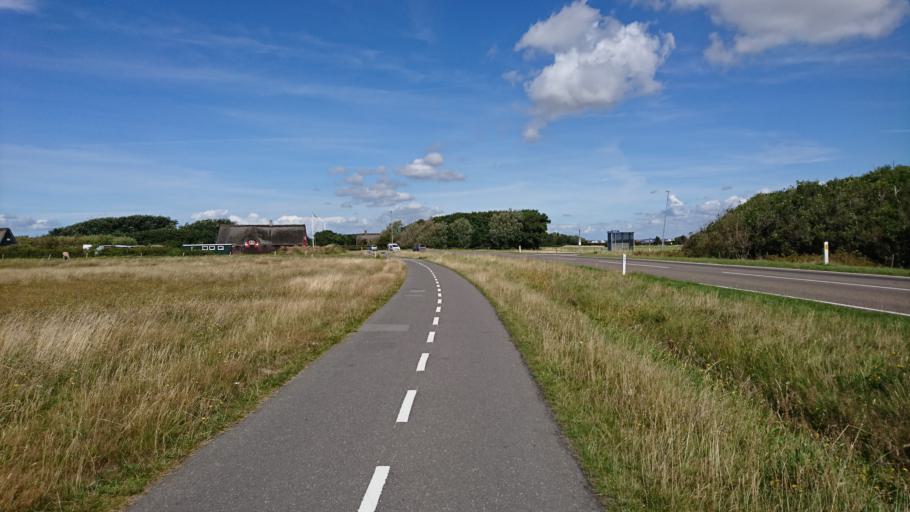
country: DK
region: South Denmark
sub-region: Fano Kommune
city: Nordby
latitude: 55.4231
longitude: 8.3992
